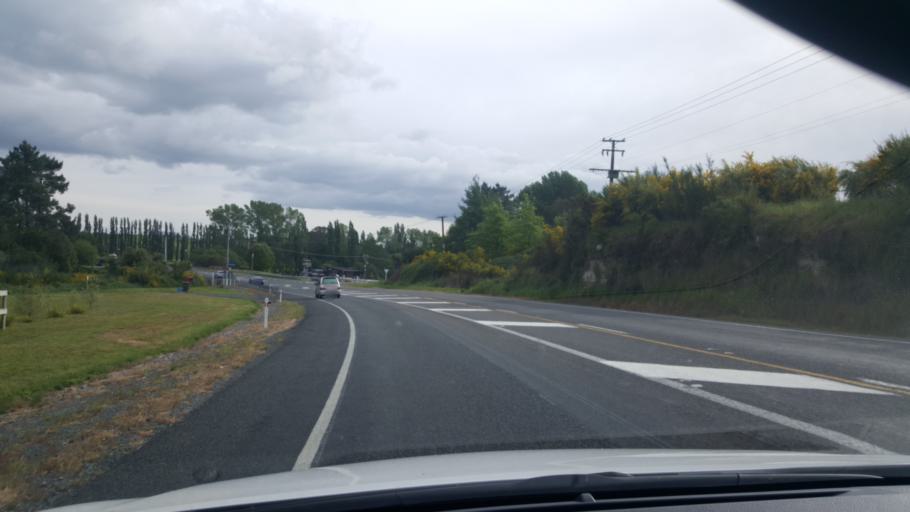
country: NZ
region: Waikato
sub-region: Taupo District
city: Taupo
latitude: -38.4830
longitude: 176.2921
